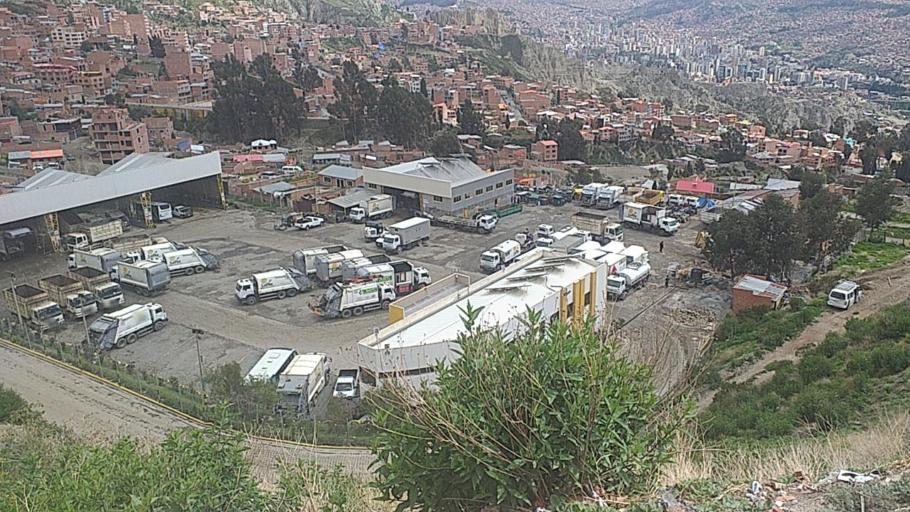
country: BO
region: La Paz
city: La Paz
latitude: -16.5390
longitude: -68.1385
